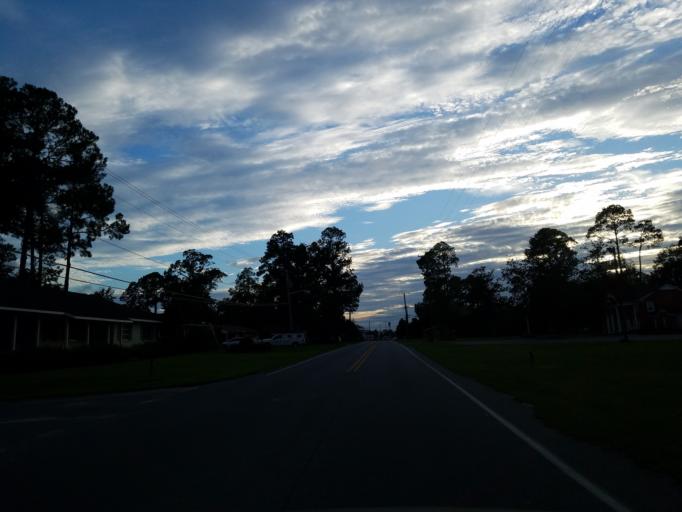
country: US
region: Georgia
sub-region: Cook County
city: Adel
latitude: 31.1482
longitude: -83.4242
